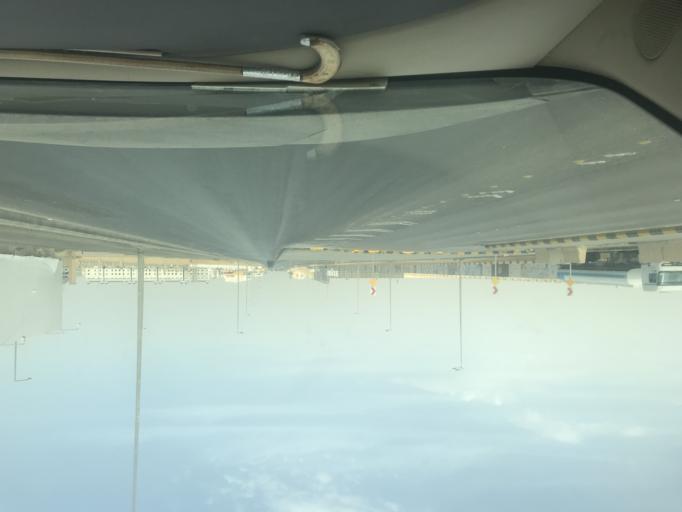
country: SA
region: Ar Riyad
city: Riyadh
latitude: 24.8123
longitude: 46.6747
